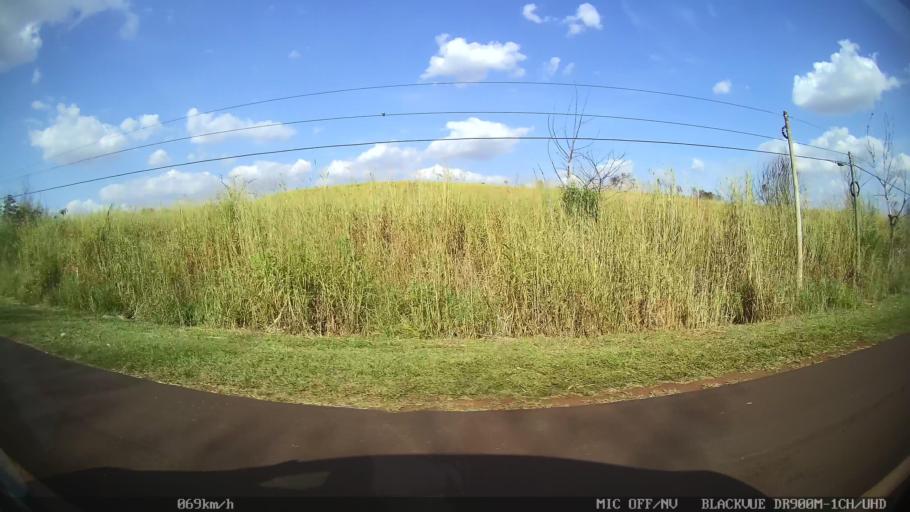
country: BR
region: Sao Paulo
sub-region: Ribeirao Preto
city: Ribeirao Preto
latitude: -21.1841
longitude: -47.8606
